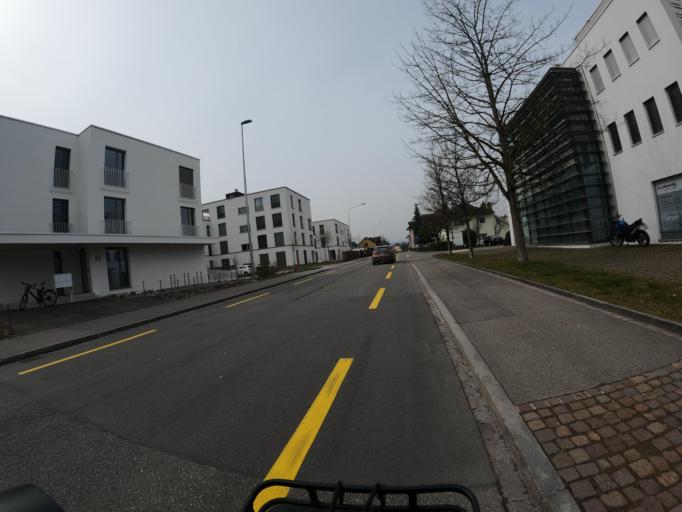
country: CH
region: Aargau
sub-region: Bezirk Aarau
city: Biberstein
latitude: 47.4047
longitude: 8.0902
